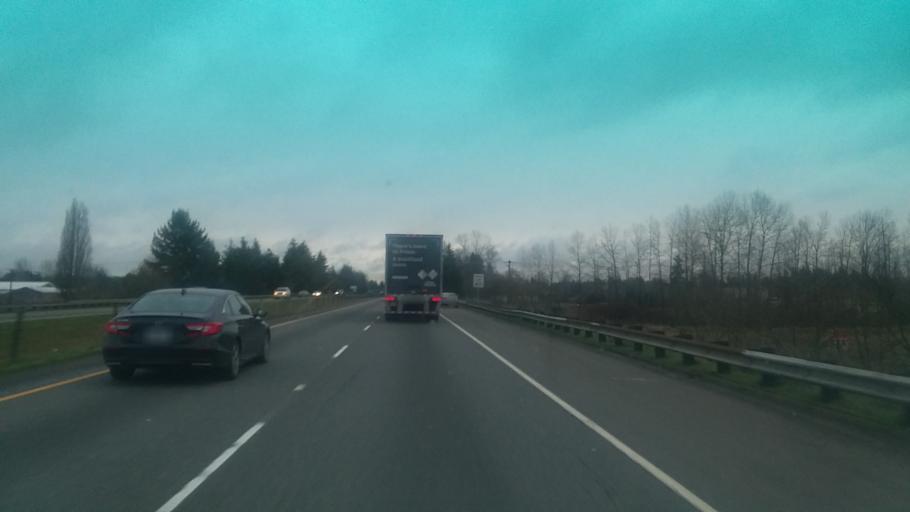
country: US
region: Washington
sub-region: Pierce County
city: Midland
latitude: 47.1581
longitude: -122.3916
